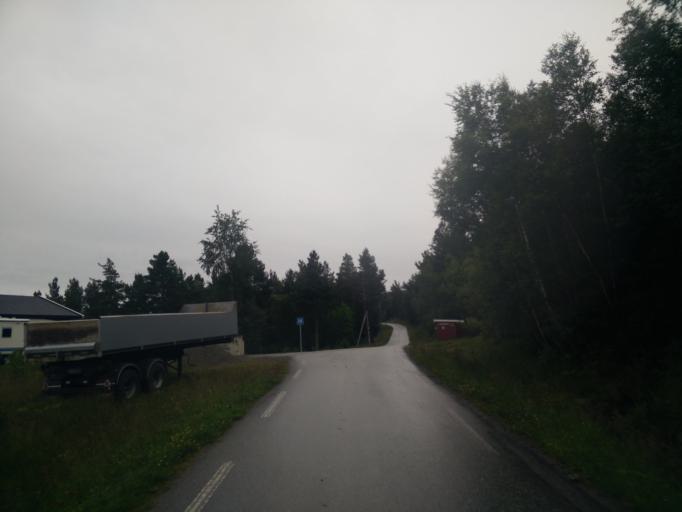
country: NO
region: More og Romsdal
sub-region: Kristiansund
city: Rensvik
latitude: 63.0235
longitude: 7.8974
